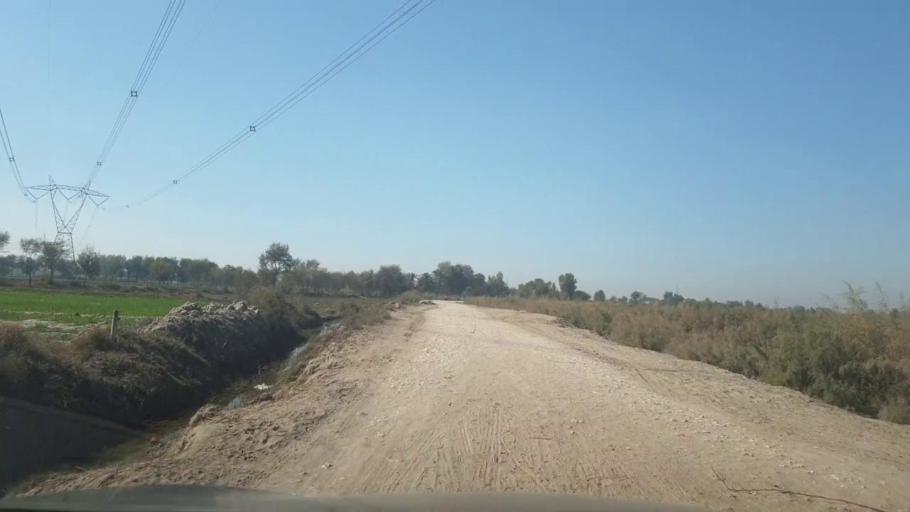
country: PK
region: Sindh
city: Adilpur
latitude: 27.8919
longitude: 69.2858
